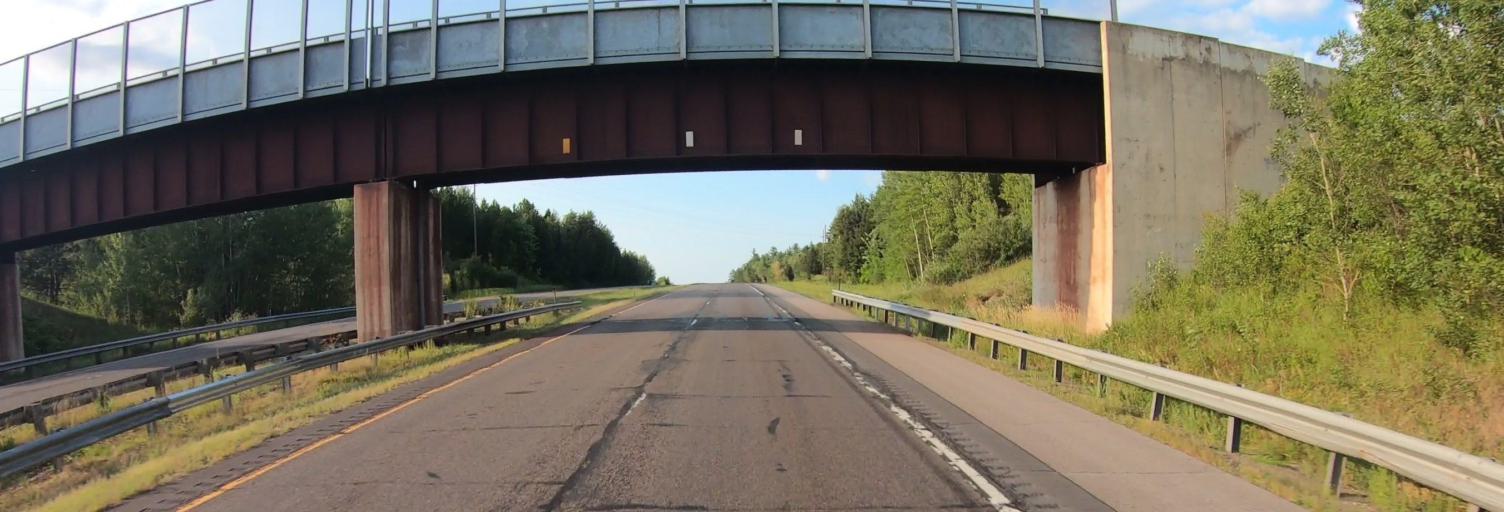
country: US
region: Minnesota
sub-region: Saint Louis County
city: Virginia
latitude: 47.5612
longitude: -92.5450
